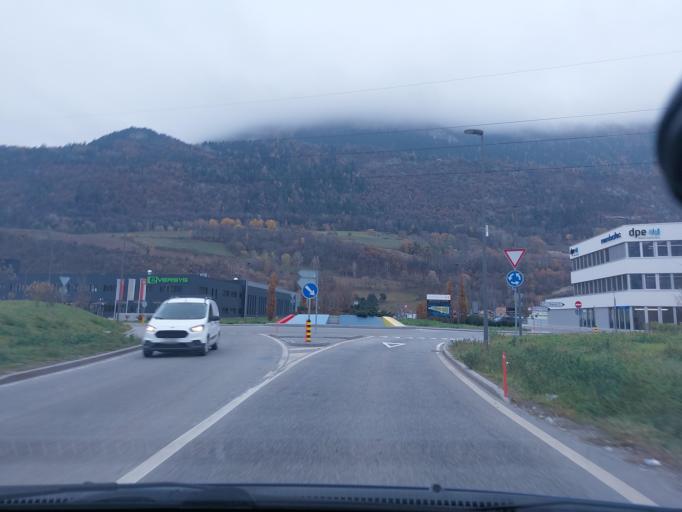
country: CH
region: Valais
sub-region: Sierre District
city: Chalais
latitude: 46.2743
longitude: 7.5174
